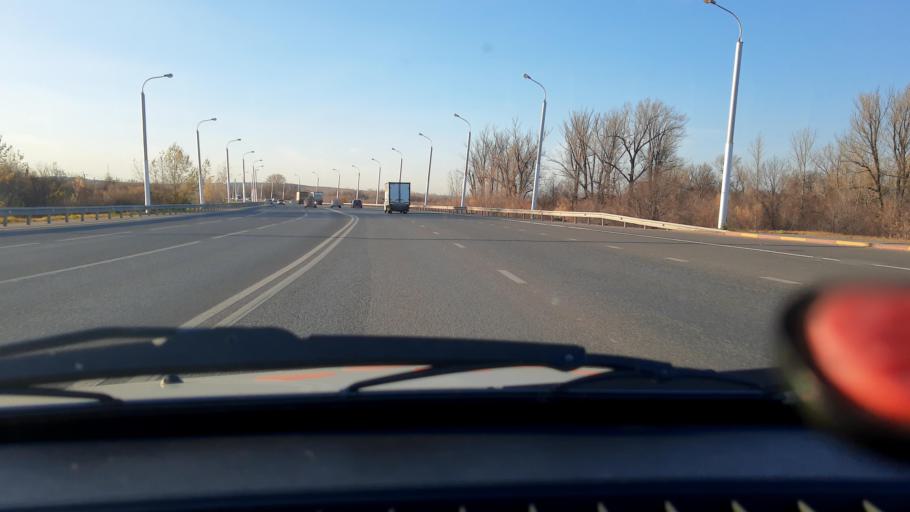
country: RU
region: Bashkortostan
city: Iglino
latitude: 54.7982
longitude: 56.2042
